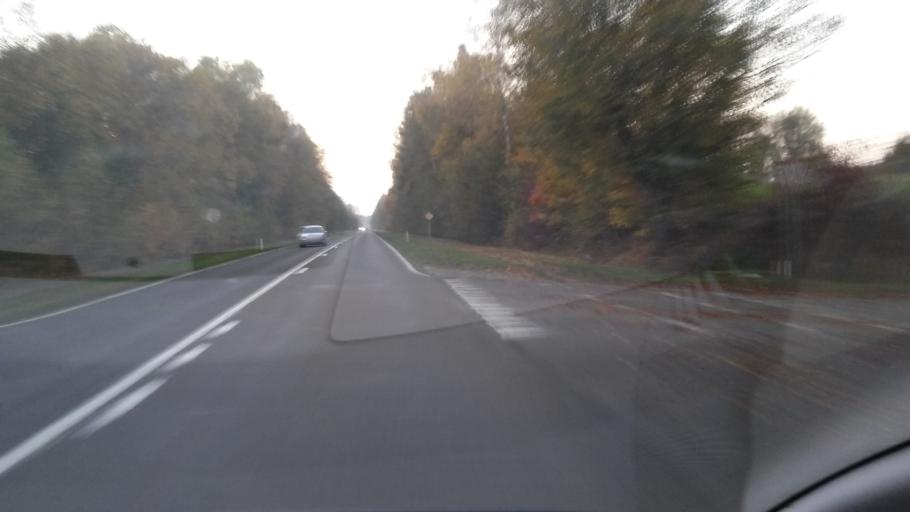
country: BE
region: Wallonia
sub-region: Province du Luxembourg
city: Etalle
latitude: 49.6704
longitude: 5.6540
